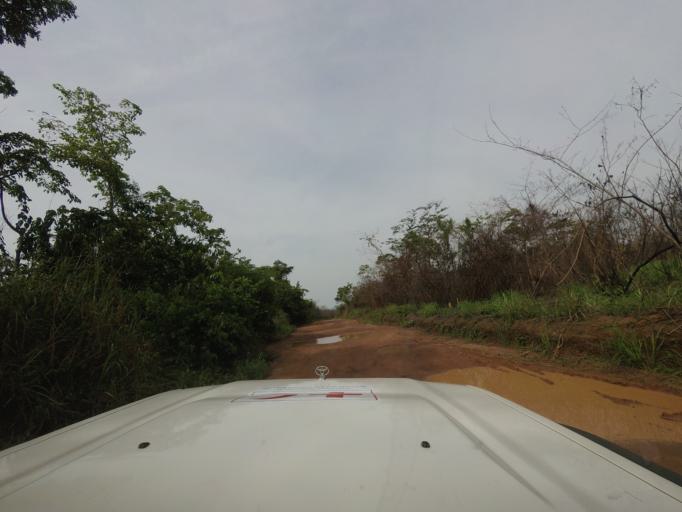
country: GN
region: Nzerekore
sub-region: Macenta
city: Macenta
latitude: 8.5175
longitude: -9.5204
